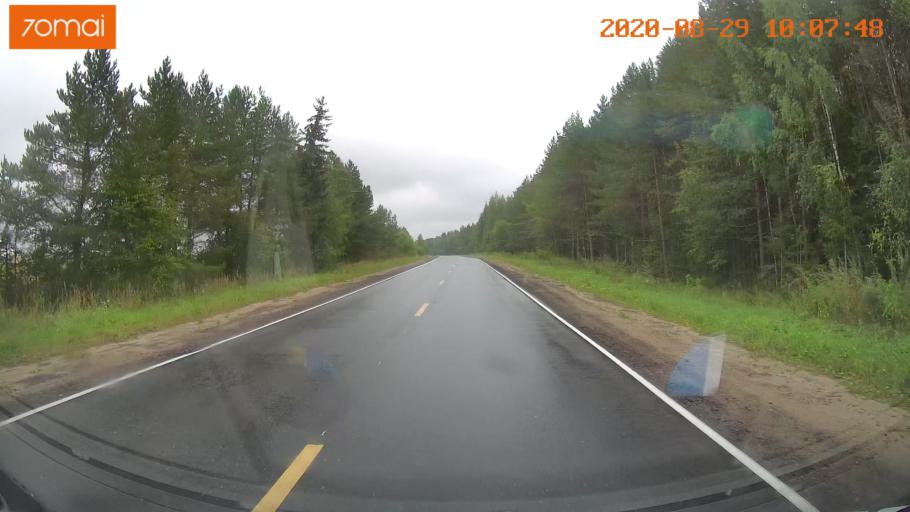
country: RU
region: Ivanovo
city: Kuznechikha
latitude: 57.3784
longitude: 42.5746
